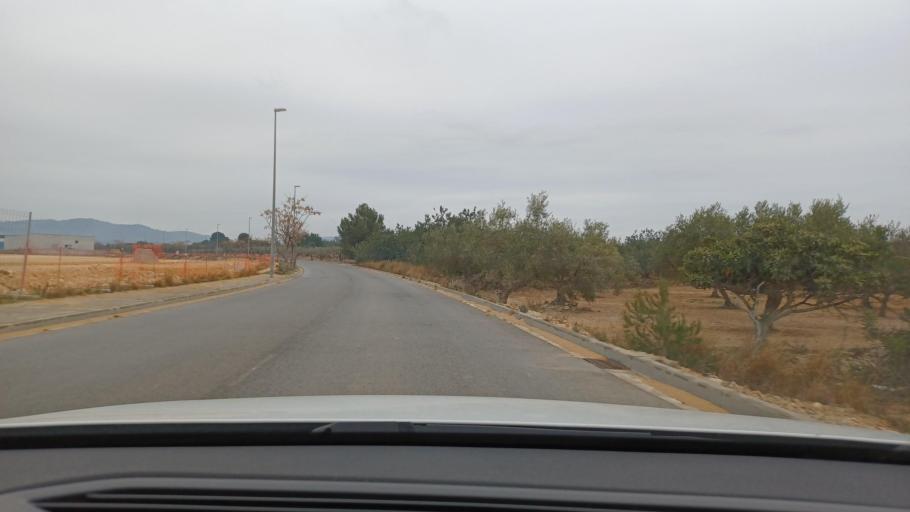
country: ES
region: Catalonia
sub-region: Provincia de Tarragona
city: Amposta
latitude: 40.7645
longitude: 0.5989
